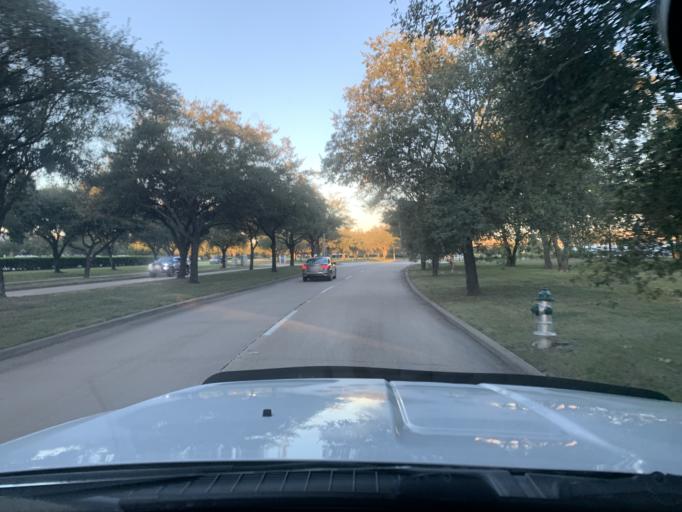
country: US
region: Texas
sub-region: Fort Bend County
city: Meadows Place
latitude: 29.6458
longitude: -95.6095
